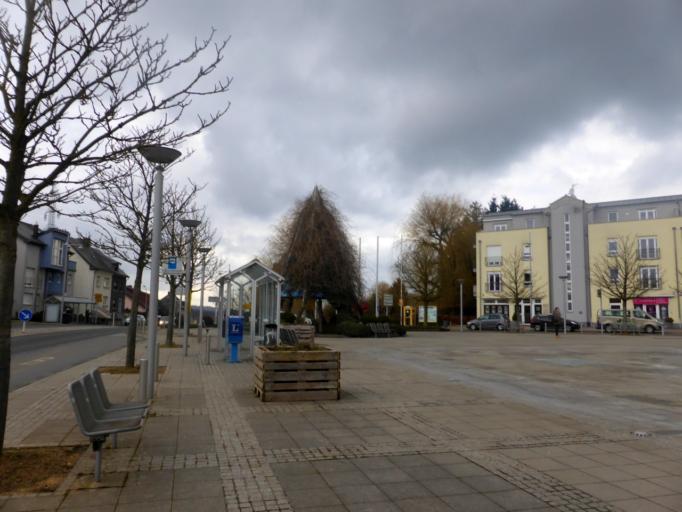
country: LU
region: Luxembourg
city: Soleuvre
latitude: 49.5216
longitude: 5.9364
